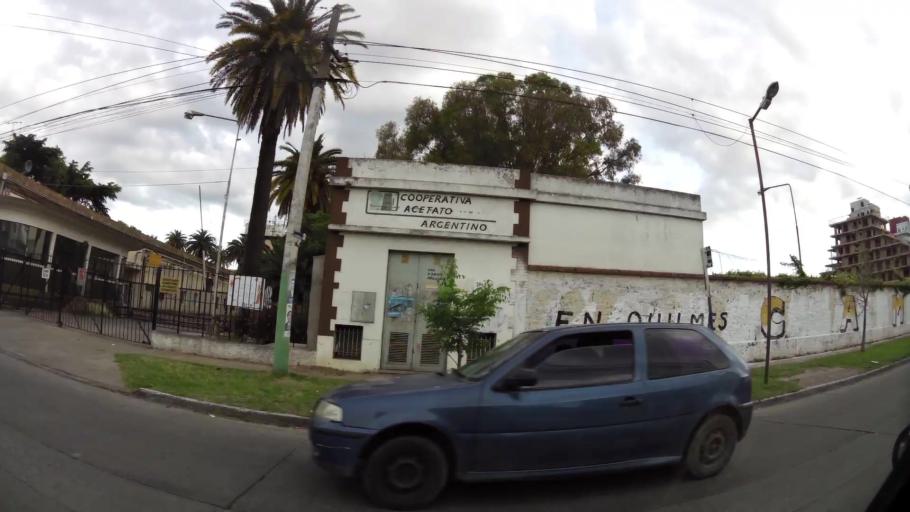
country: AR
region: Buenos Aires
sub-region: Partido de Quilmes
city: Quilmes
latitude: -34.7297
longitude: -58.2437
